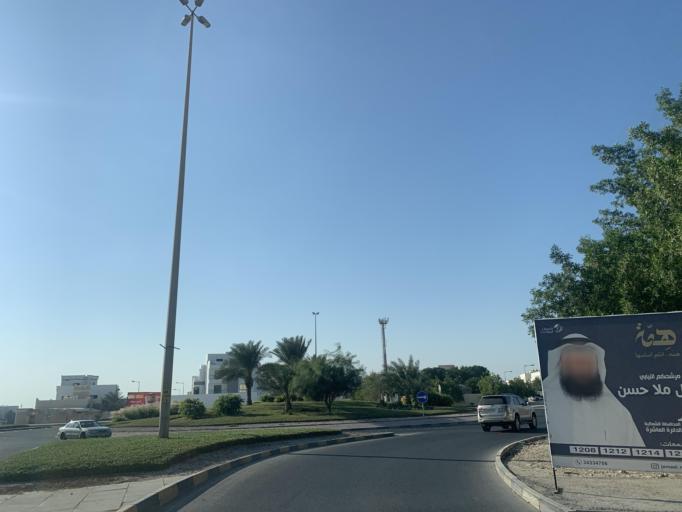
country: BH
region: Central Governorate
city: Madinat Hamad
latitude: 26.1109
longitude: 50.5049
